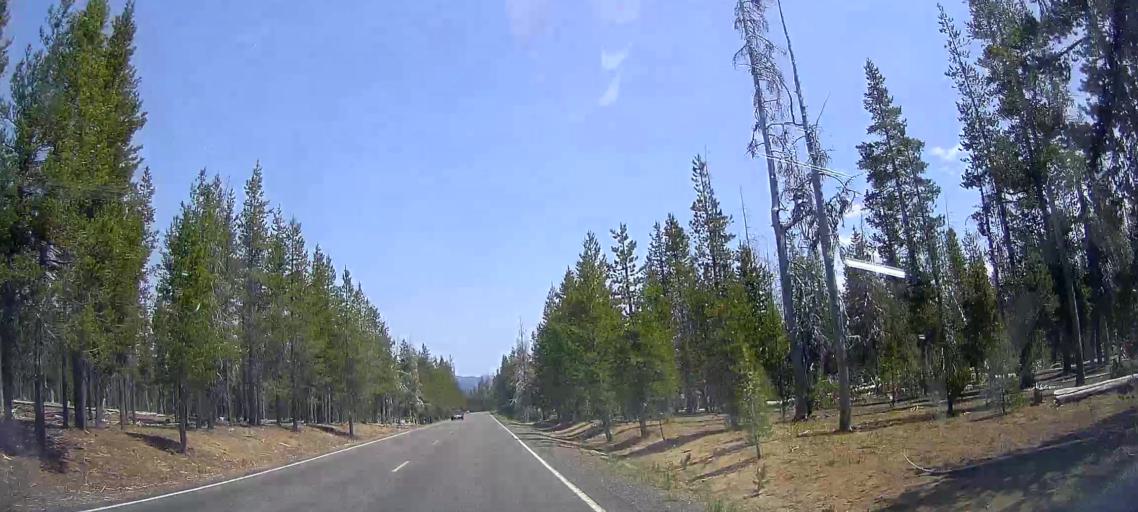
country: US
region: Oregon
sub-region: Lane County
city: Oakridge
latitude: 43.0211
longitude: -122.1230
